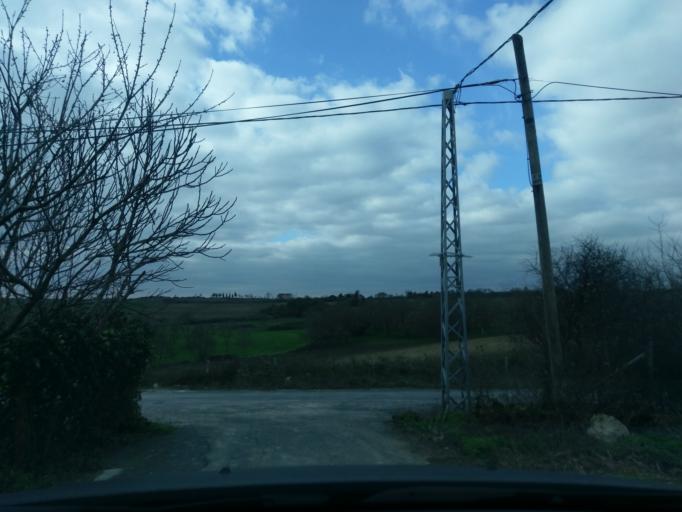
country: TR
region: Istanbul
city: Boyalik
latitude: 41.2721
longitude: 28.6568
